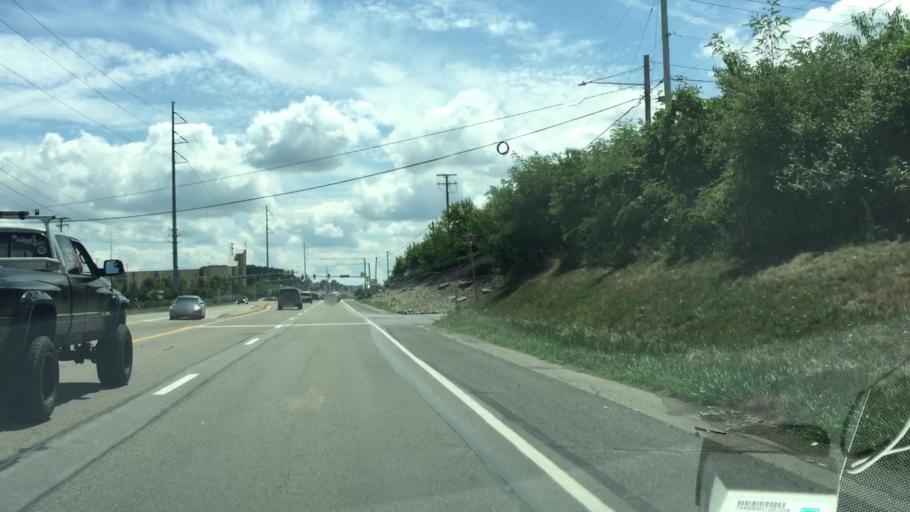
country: US
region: Pennsylvania
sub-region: Butler County
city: Fox Run
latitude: 40.7421
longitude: -80.1126
